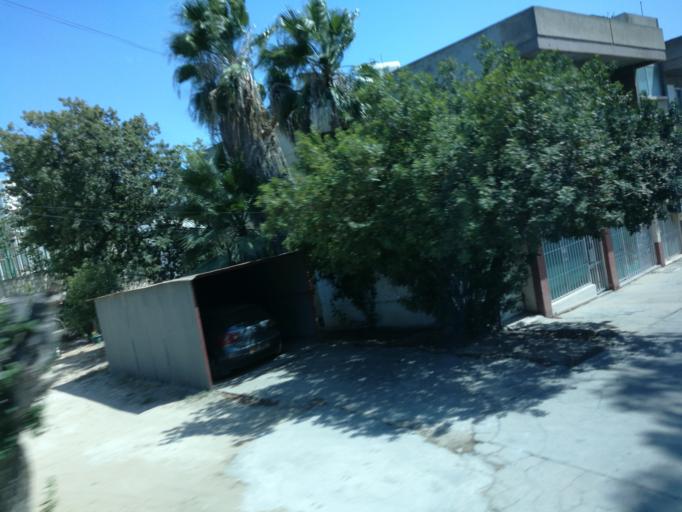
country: CY
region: Ammochostos
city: Famagusta
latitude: 35.1136
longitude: 33.9448
